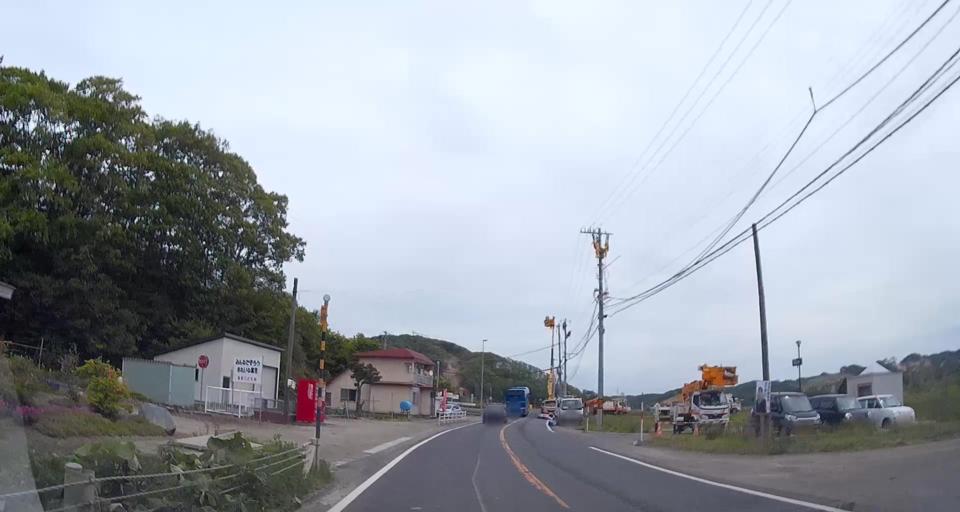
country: JP
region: Hokkaido
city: Chitose
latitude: 42.7585
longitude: 141.9252
